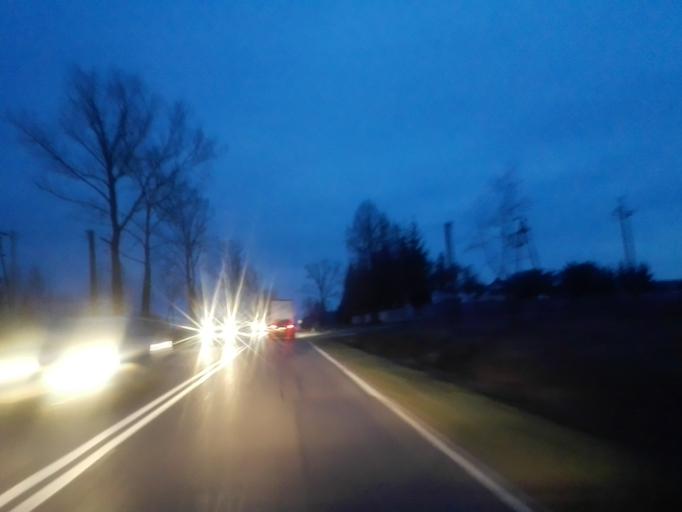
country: PL
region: Podlasie
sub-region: Lomza
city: Lomza
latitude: 53.1091
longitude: 22.0288
